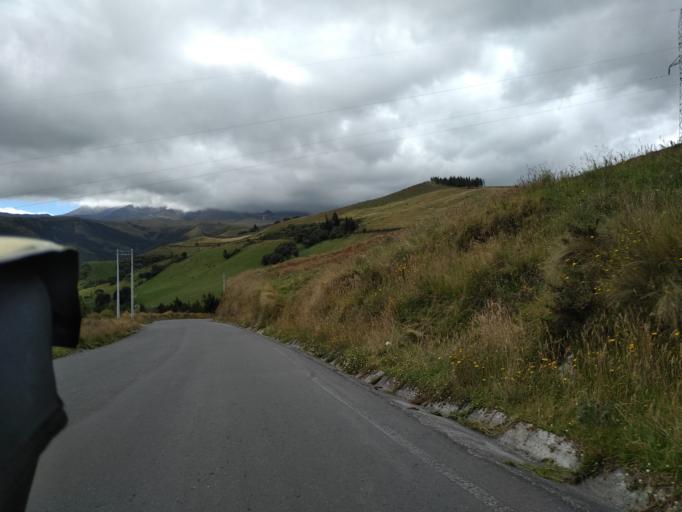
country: EC
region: Cotopaxi
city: Saquisili
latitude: -0.7337
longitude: -78.7545
